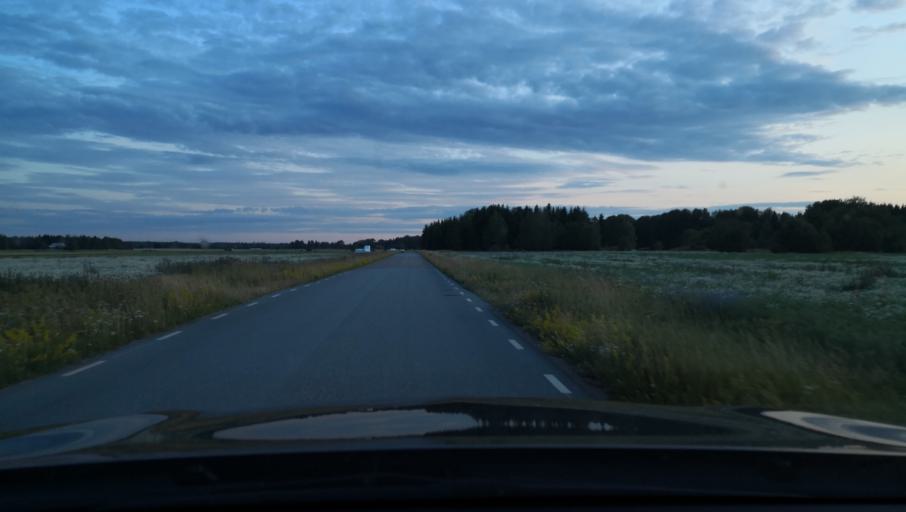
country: SE
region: Uppsala
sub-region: Osthammars Kommun
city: Bjorklinge
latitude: 60.0497
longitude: 17.5129
